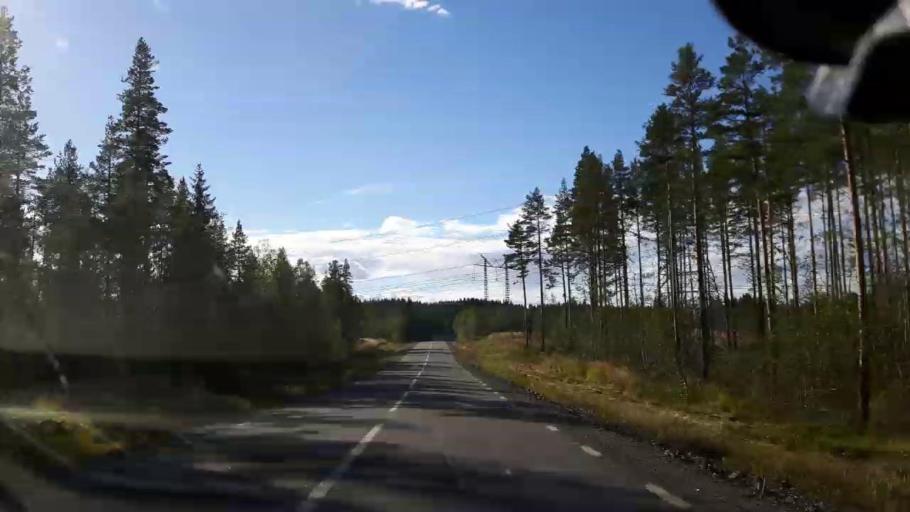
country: SE
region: Jaemtland
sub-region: Ragunda Kommun
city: Hammarstrand
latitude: 63.5331
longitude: 16.0560
